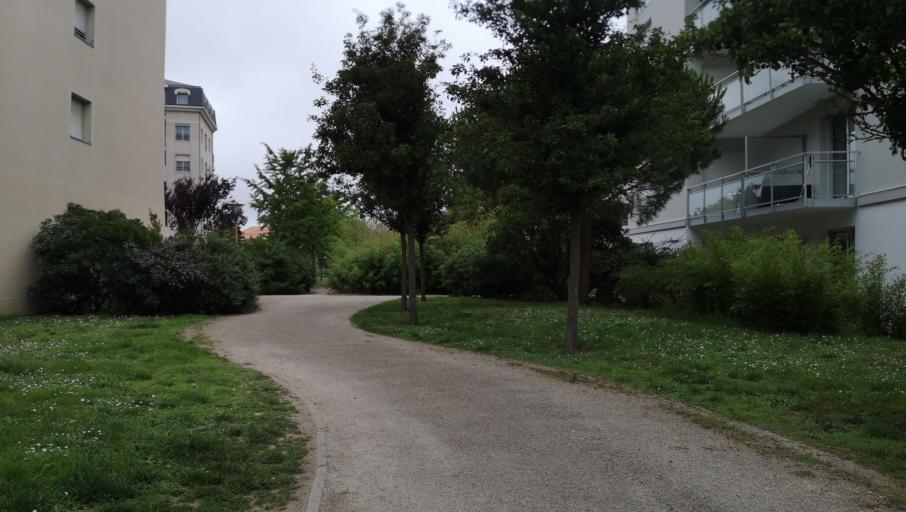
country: FR
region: Pays de la Loire
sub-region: Departement de la Vendee
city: Les Sables-d'Olonne
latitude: 46.4995
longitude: -1.7833
